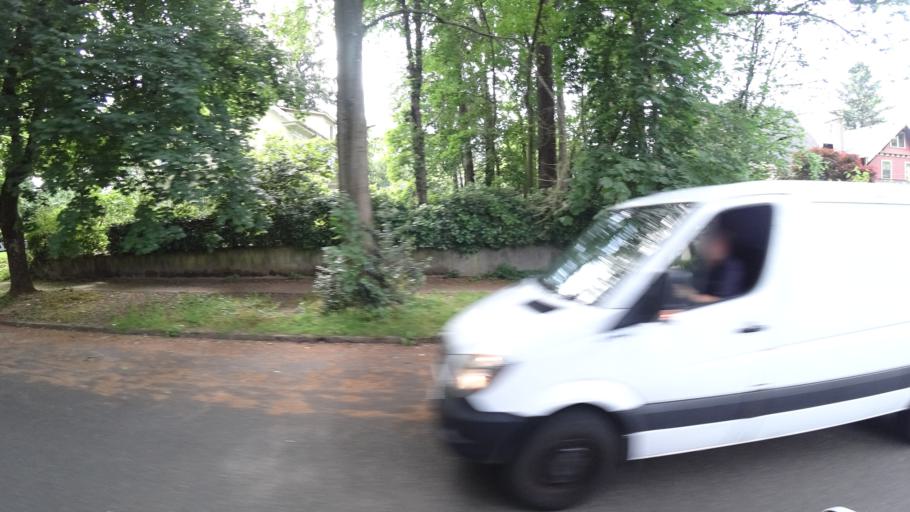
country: US
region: Oregon
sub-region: Multnomah County
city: Portland
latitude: 45.5455
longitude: -122.6484
